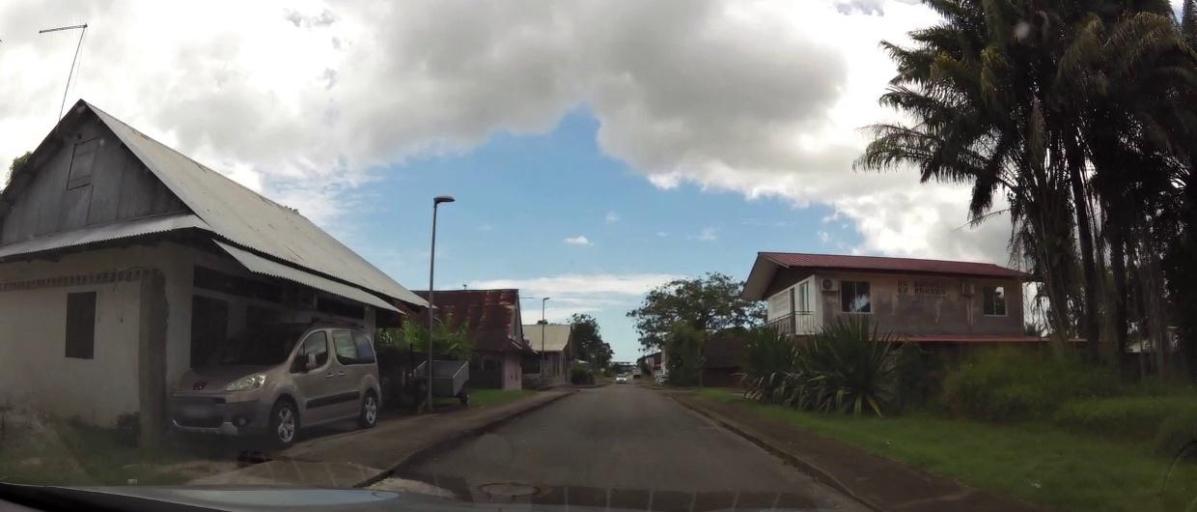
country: GF
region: Guyane
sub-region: Guyane
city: Sinnamary
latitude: 5.3750
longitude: -52.9574
